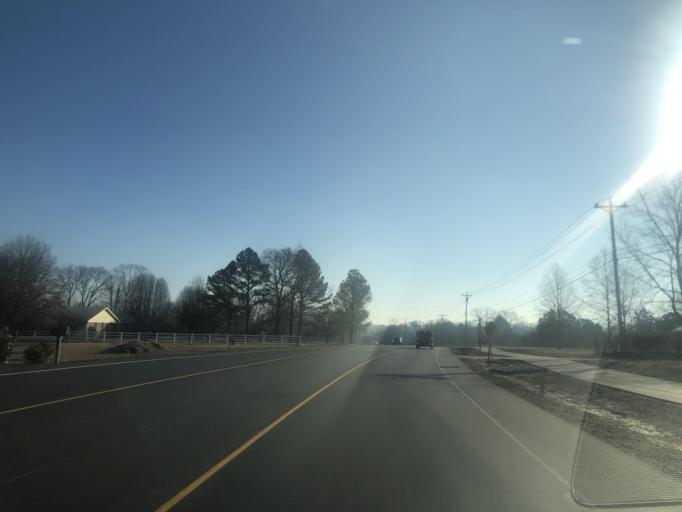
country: US
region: Tennessee
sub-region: Williamson County
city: Nolensville
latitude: 35.9619
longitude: -86.6867
